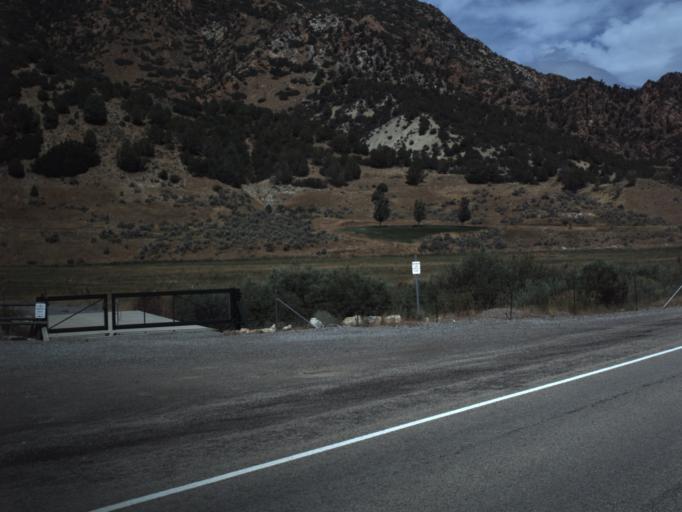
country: US
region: Utah
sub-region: Utah County
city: Woodland Hills
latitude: 39.9799
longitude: -111.5030
